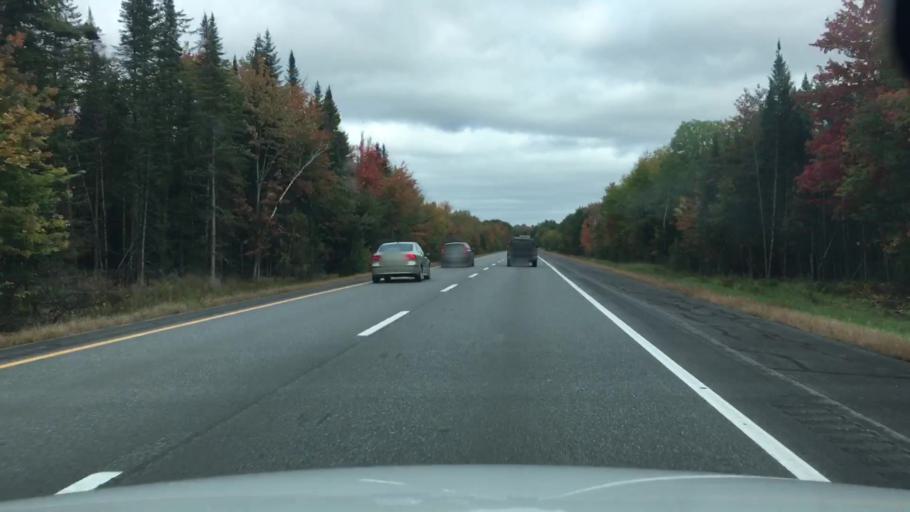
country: US
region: Maine
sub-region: Somerset County
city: Pittsfield
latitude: 44.8091
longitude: -69.3575
